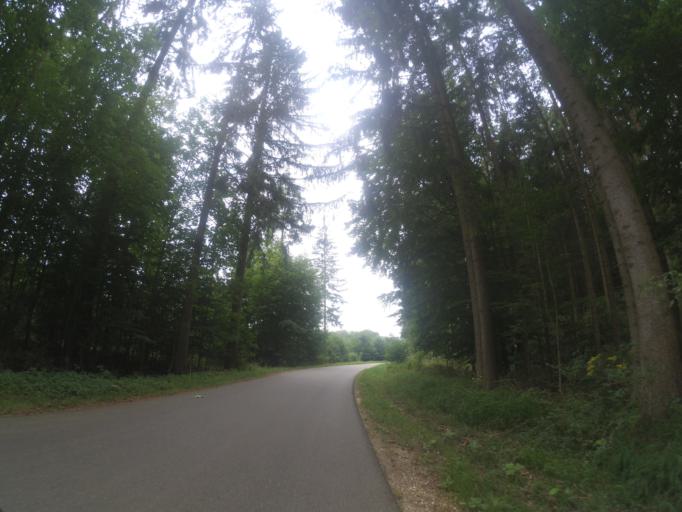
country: DE
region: Baden-Wuerttemberg
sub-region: Tuebingen Region
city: Westerstetten
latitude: 48.5130
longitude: 9.9385
